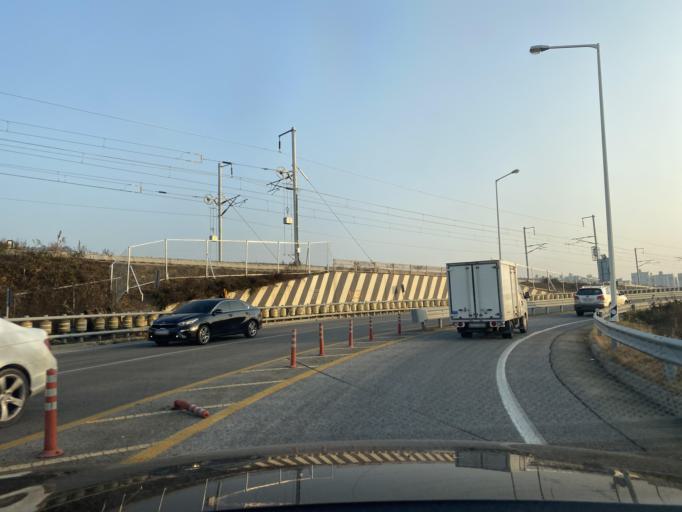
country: KR
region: Chungcheongnam-do
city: Yesan
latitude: 36.7050
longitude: 126.8313
